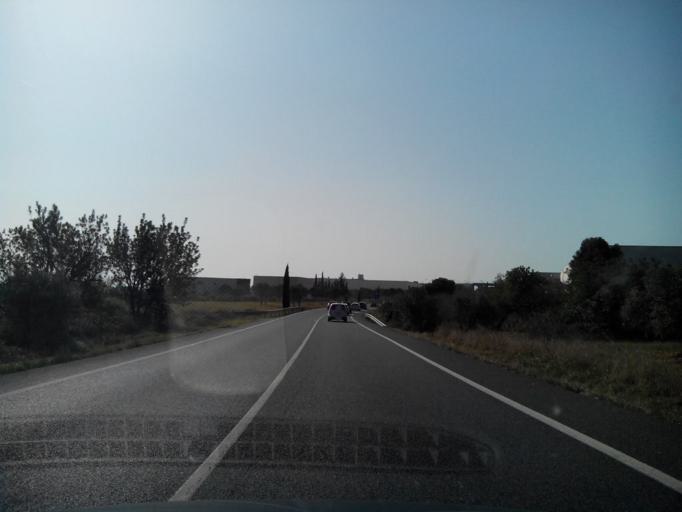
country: ES
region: Catalonia
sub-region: Provincia de Tarragona
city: Alcover
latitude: 41.2837
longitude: 1.1837
